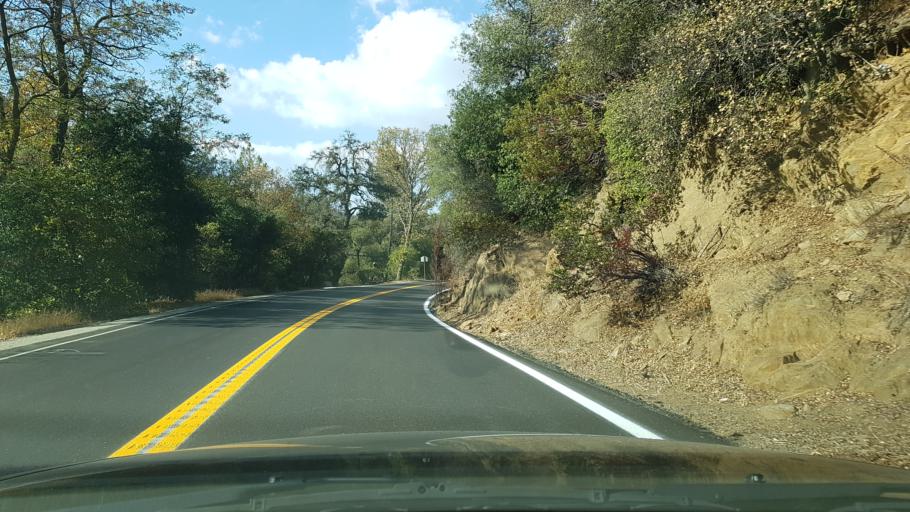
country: US
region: California
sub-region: San Diego County
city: Julian
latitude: 33.0824
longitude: -116.5892
